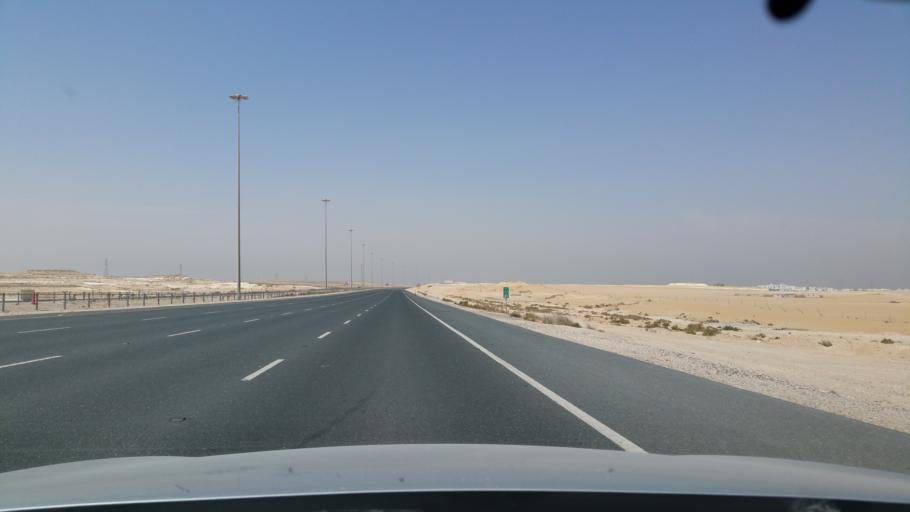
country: QA
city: Umm Bab
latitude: 24.8579
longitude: 50.8973
